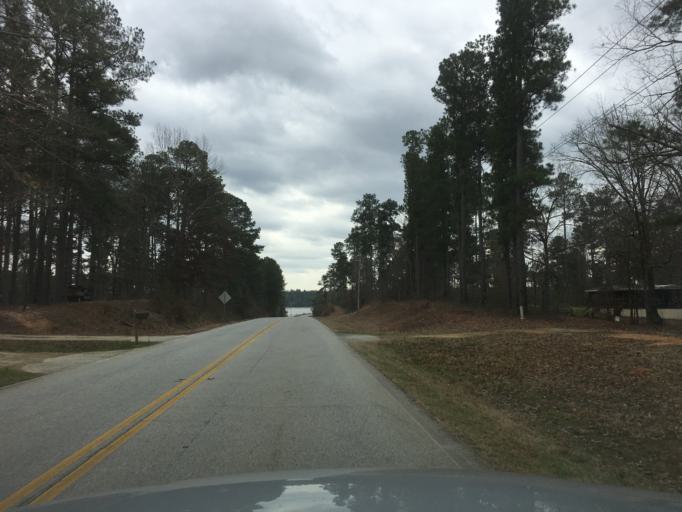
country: US
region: Georgia
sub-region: Lincoln County
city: Lincolnton
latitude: 33.8334
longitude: -82.4090
